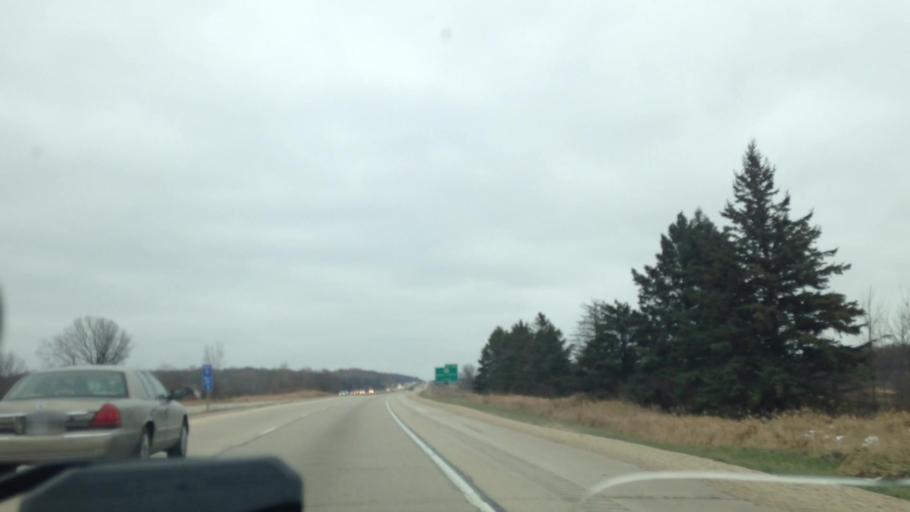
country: US
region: Wisconsin
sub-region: Washington County
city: Slinger
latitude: 43.3889
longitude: -88.3117
